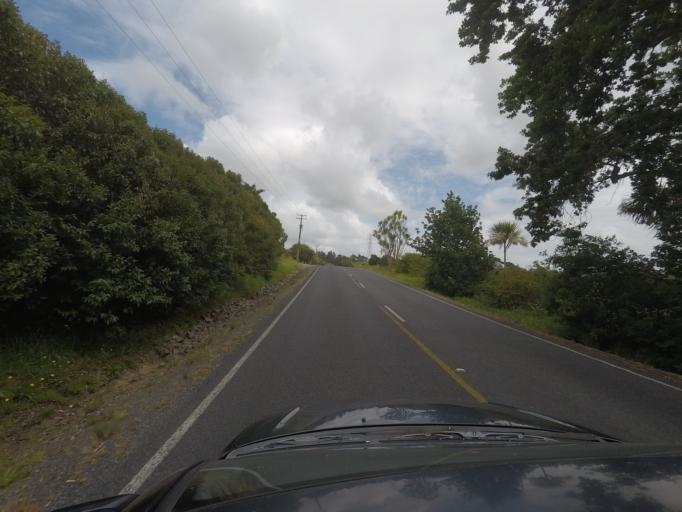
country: NZ
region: Auckland
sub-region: Auckland
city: Parakai
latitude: -36.6304
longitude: 174.5032
